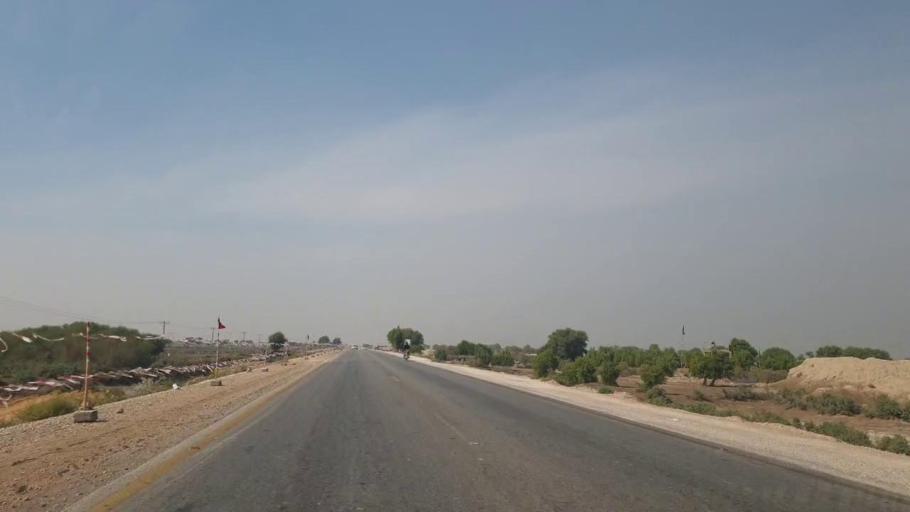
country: PK
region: Sindh
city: Sann
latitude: 25.9952
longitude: 68.1694
